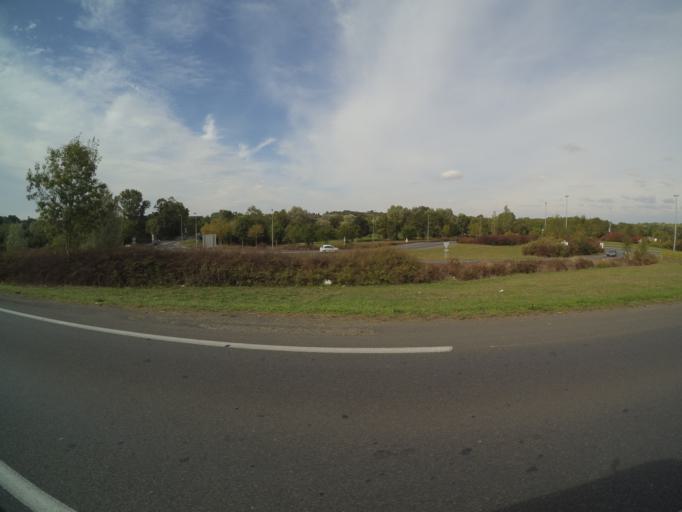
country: FR
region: Pays de la Loire
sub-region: Departement de Maine-et-Loire
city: Saumur
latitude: 47.2645
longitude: -0.0941
